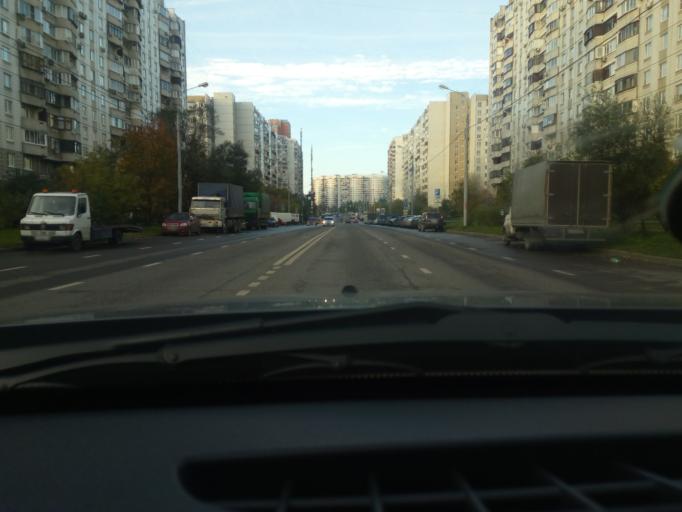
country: RU
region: Moskovskaya
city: Kuskovo
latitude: 55.7323
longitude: 37.8547
